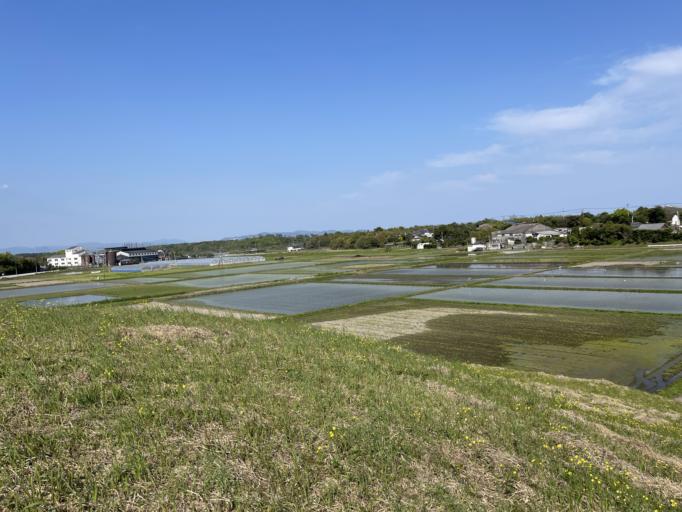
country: JP
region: Kagoshima
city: Shibushi
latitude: 31.4136
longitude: 131.0151
